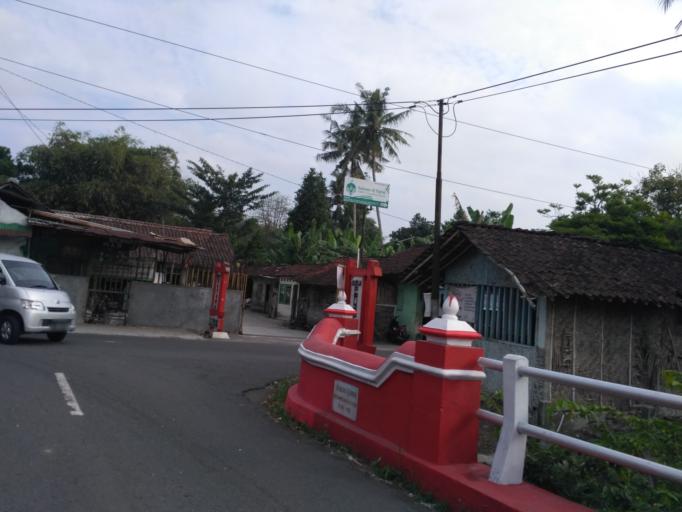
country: ID
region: Daerah Istimewa Yogyakarta
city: Melati
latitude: -7.7092
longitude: 110.3916
